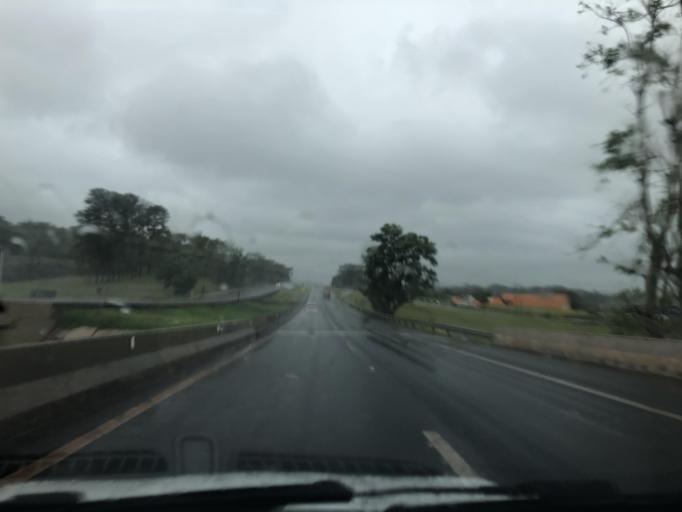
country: BR
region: Sao Paulo
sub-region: Ribeirao Preto
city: Ribeirao Preto
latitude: -21.2373
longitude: -47.7589
